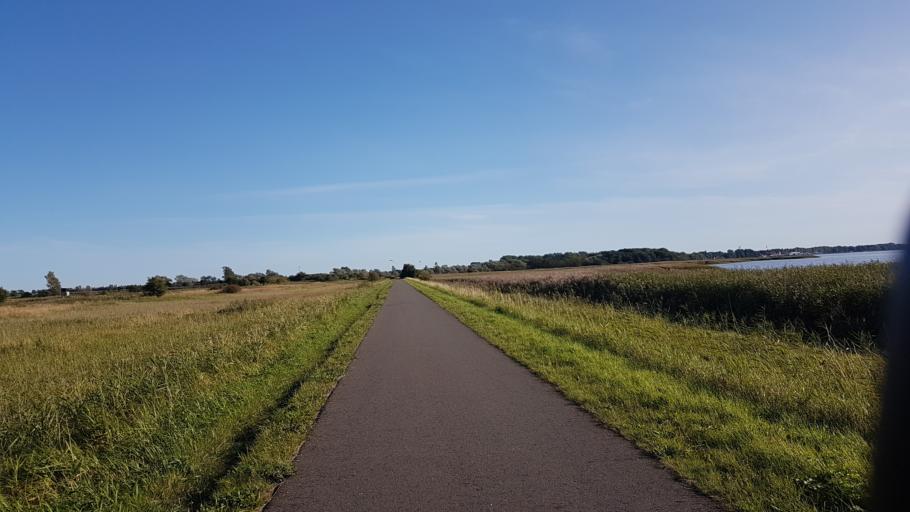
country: DE
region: Mecklenburg-Vorpommern
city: Wiek
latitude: 54.6430
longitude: 13.2868
